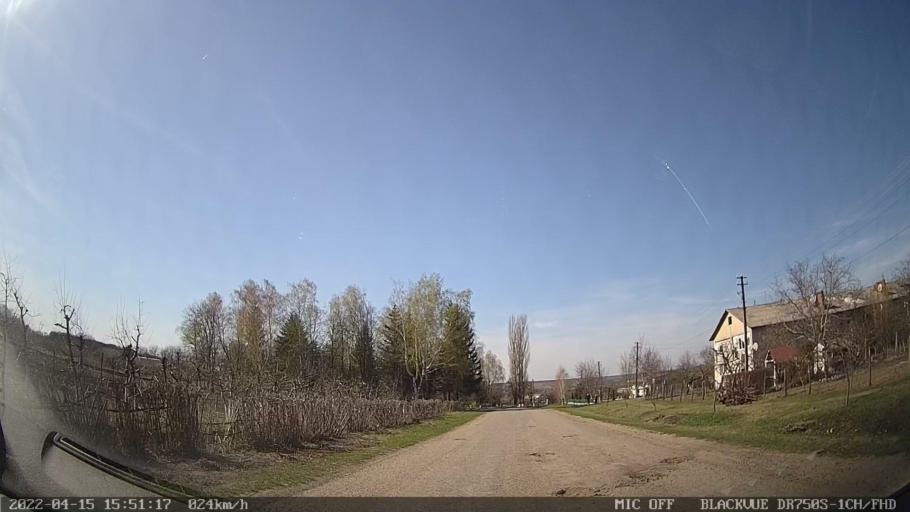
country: MD
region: Raionul Ocnita
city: Otaci
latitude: 48.3938
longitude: 27.8988
